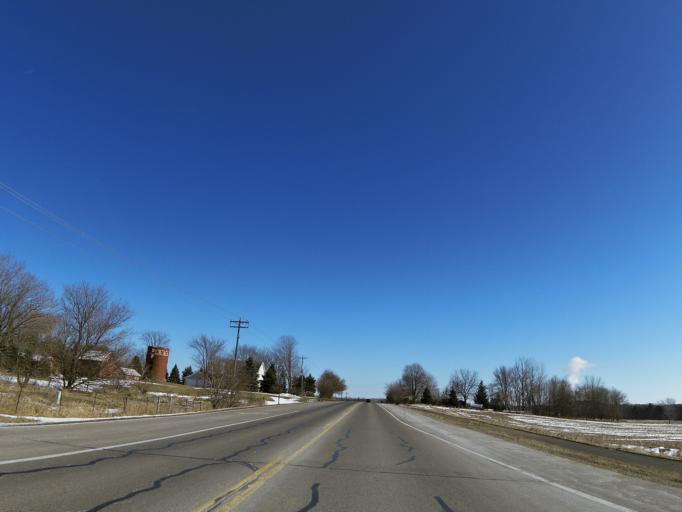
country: US
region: Minnesota
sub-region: Washington County
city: Grant
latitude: 45.0578
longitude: -92.8757
